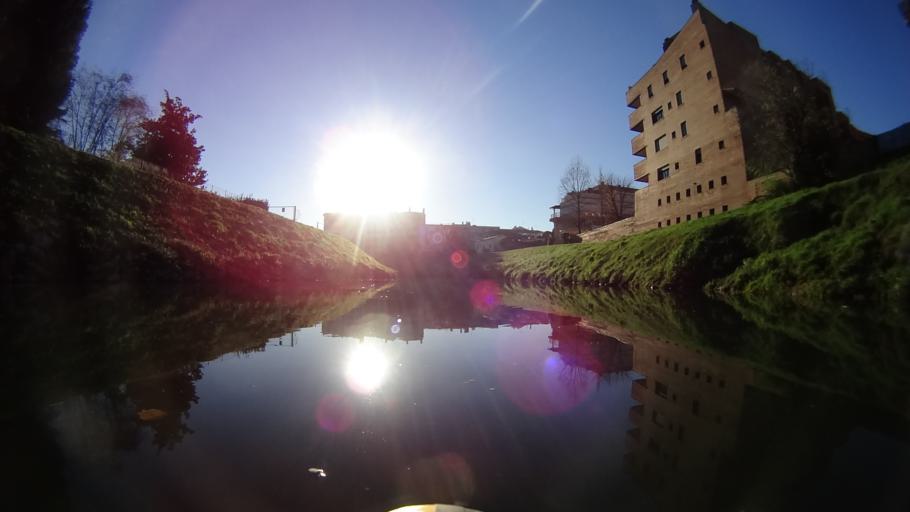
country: IT
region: Veneto
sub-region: Provincia di Vicenza
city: Vicenza
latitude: 45.5552
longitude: 11.5337
